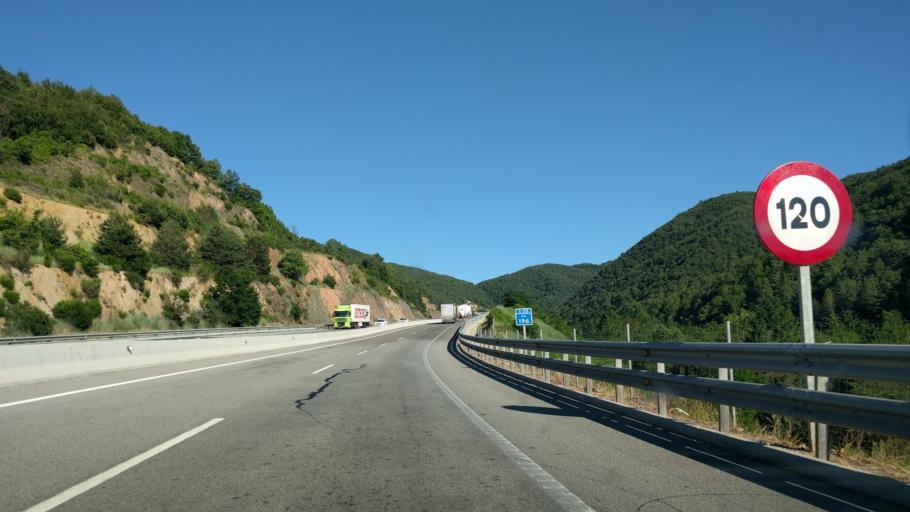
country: ES
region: Catalonia
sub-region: Provincia de Girona
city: Viladrau
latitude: 41.8932
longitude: 2.3781
